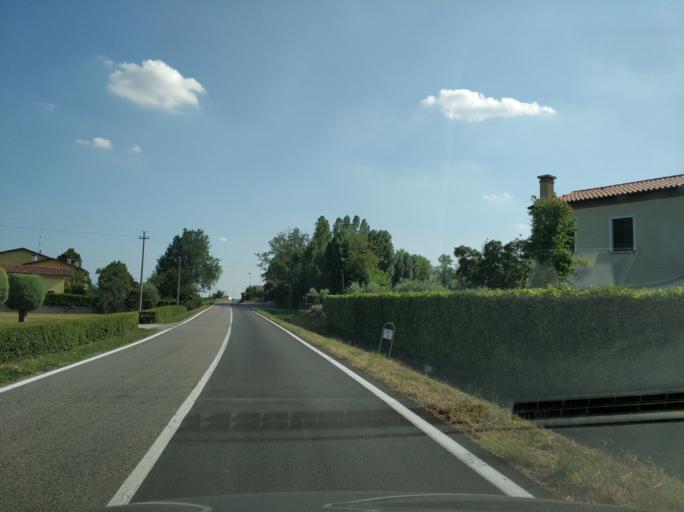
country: IT
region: Veneto
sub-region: Provincia di Padova
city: Arqua Petrarca
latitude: 45.2453
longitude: 11.7117
